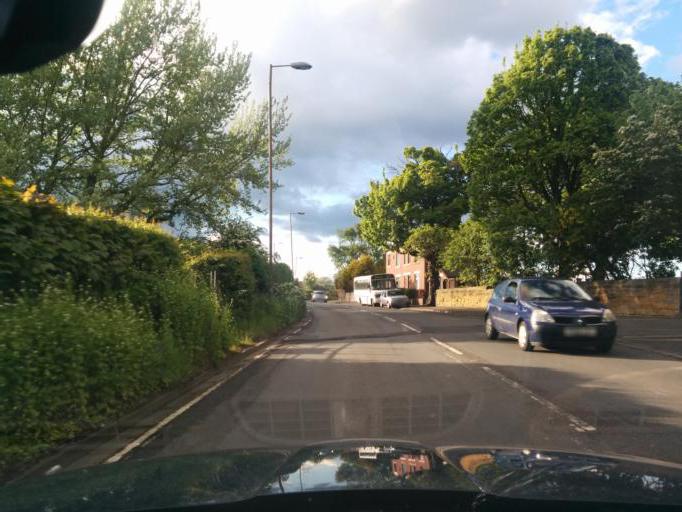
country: GB
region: England
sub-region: Northumberland
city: Choppington
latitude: 55.1553
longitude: -1.6037
